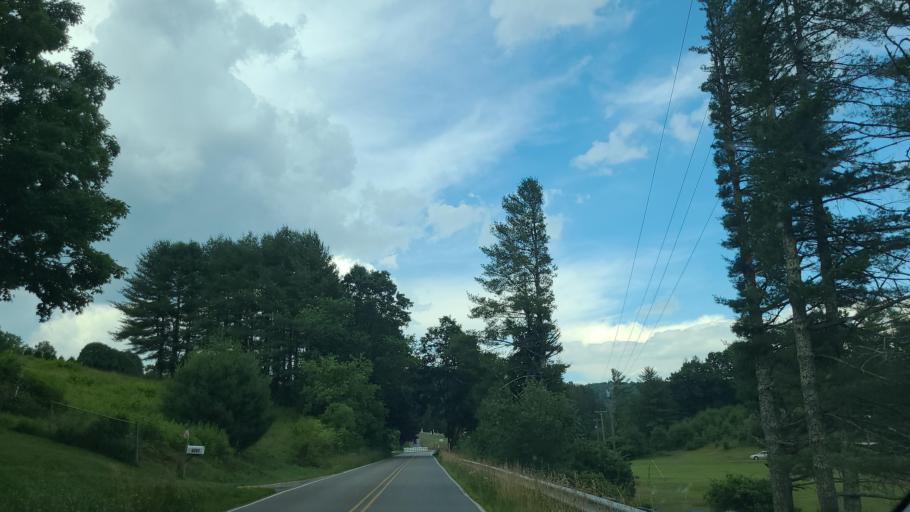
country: US
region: North Carolina
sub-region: Ashe County
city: Jefferson
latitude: 36.3898
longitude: -81.3603
